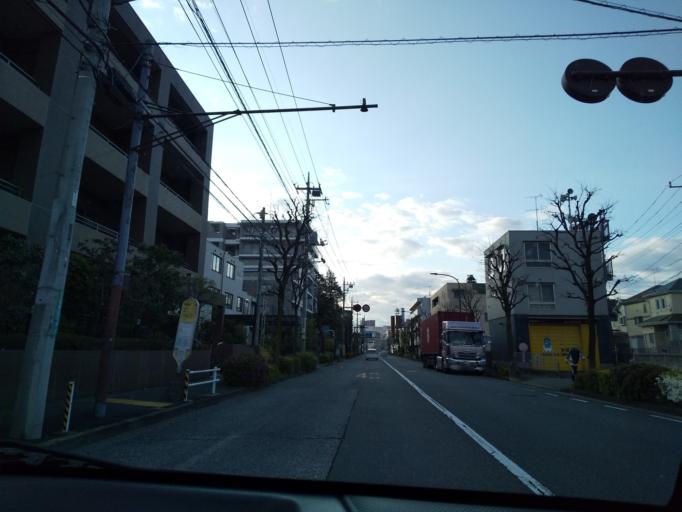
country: JP
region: Tokyo
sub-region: Machida-shi
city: Machida
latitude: 35.5497
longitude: 139.4346
